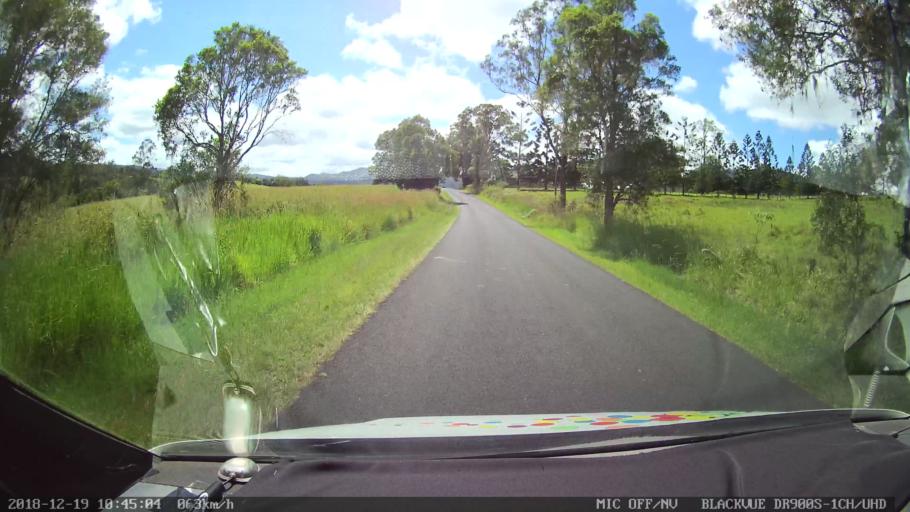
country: AU
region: New South Wales
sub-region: Lismore Municipality
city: Nimbin
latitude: -28.5960
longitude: 153.1867
